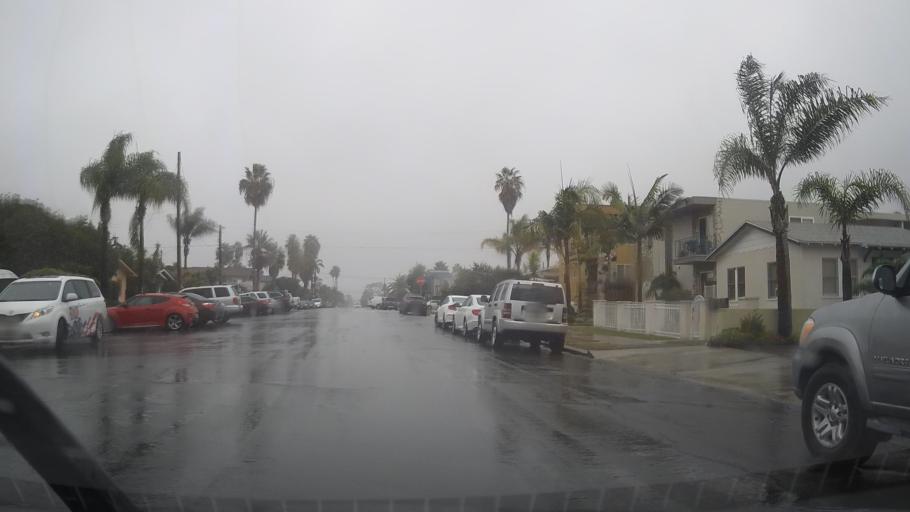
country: US
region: California
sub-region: San Diego County
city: San Diego
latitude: 32.7495
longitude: -117.1376
